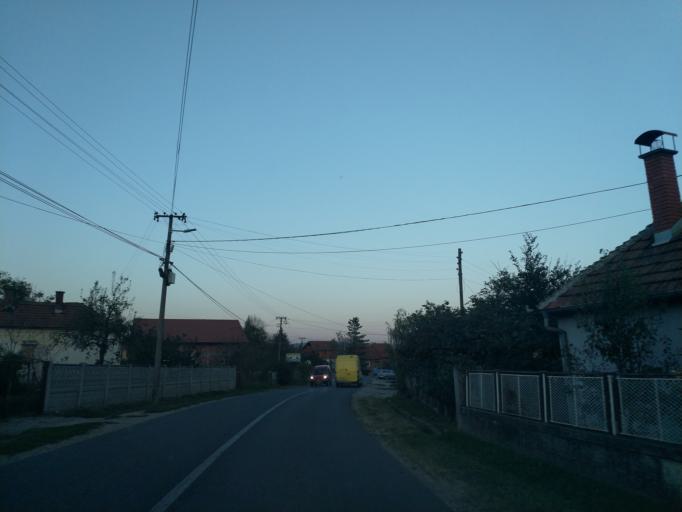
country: RS
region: Central Serbia
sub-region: Rasinski Okrug
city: Krusevac
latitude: 43.6091
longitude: 21.2900
